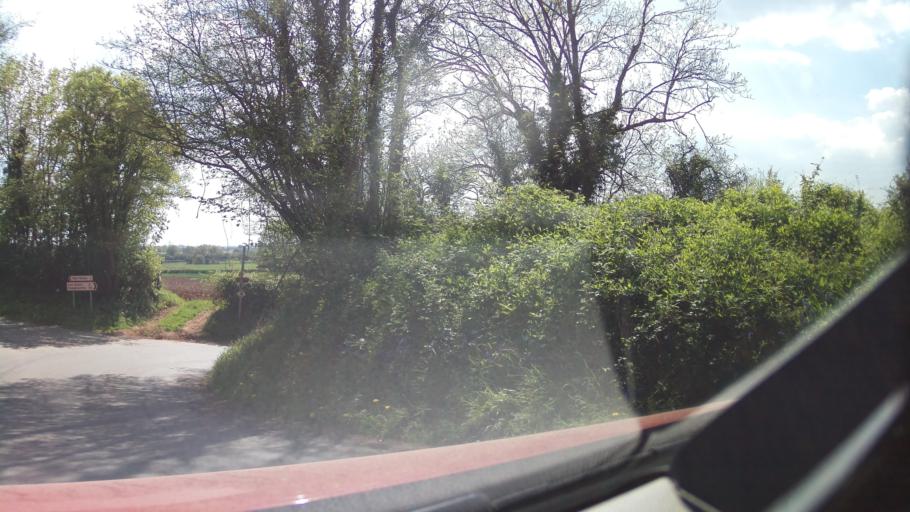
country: GB
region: England
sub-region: South Gloucestershire
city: Yate
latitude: 51.5664
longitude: -2.4069
